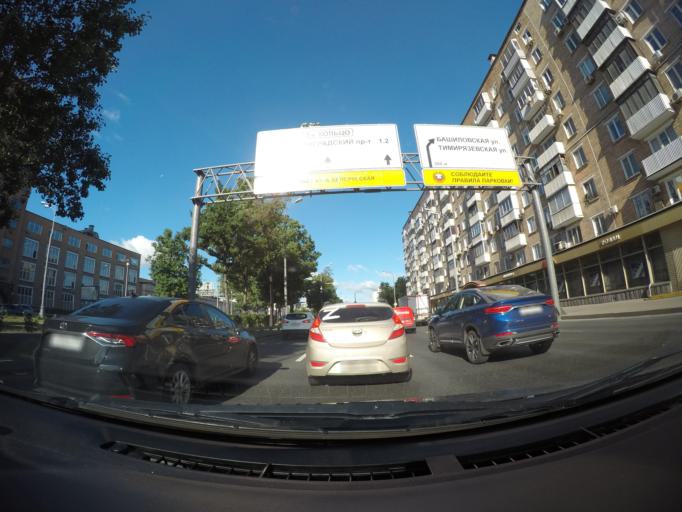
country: RU
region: Moscow
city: Mar'ina Roshcha
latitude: 55.7922
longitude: 37.5814
